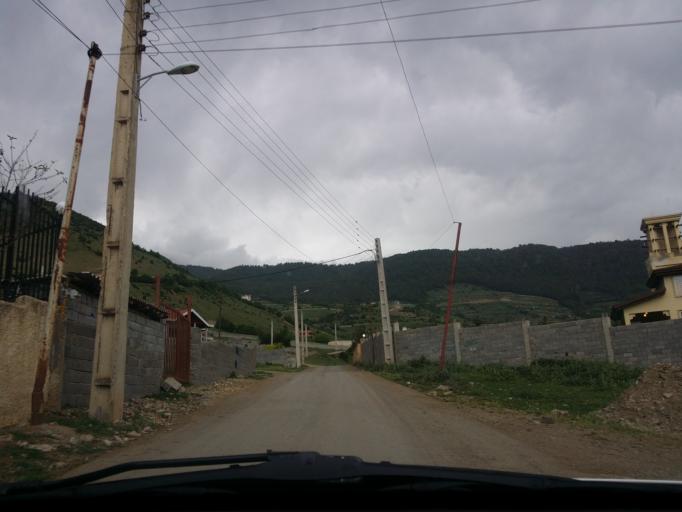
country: IR
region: Mazandaran
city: `Abbasabad
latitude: 36.5064
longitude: 51.1419
